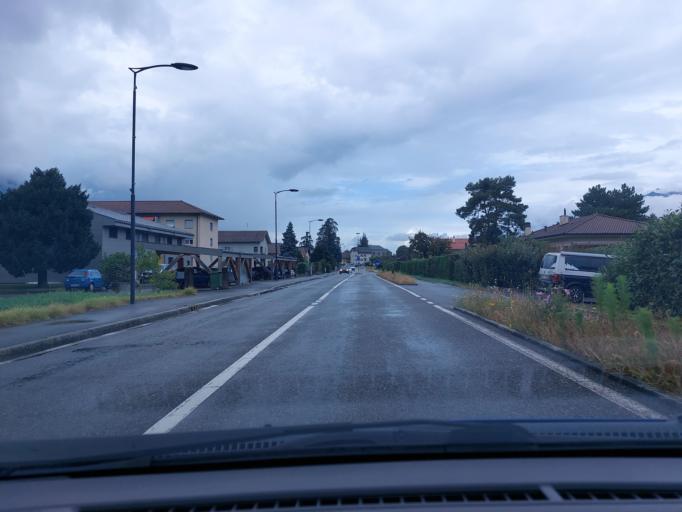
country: CH
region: Vaud
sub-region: Aigle District
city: Bex
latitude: 46.2396
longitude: 6.9917
